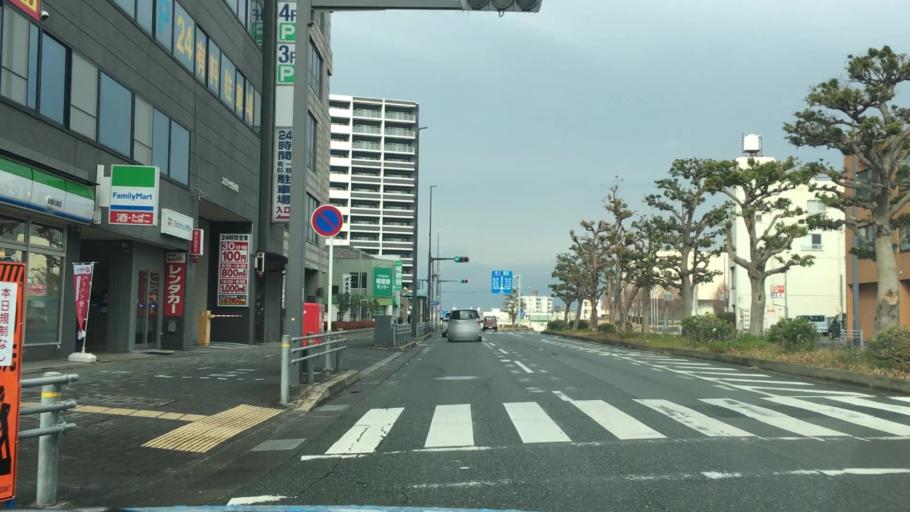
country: JP
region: Aichi
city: Toyohashi
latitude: 34.7668
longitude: 137.3829
